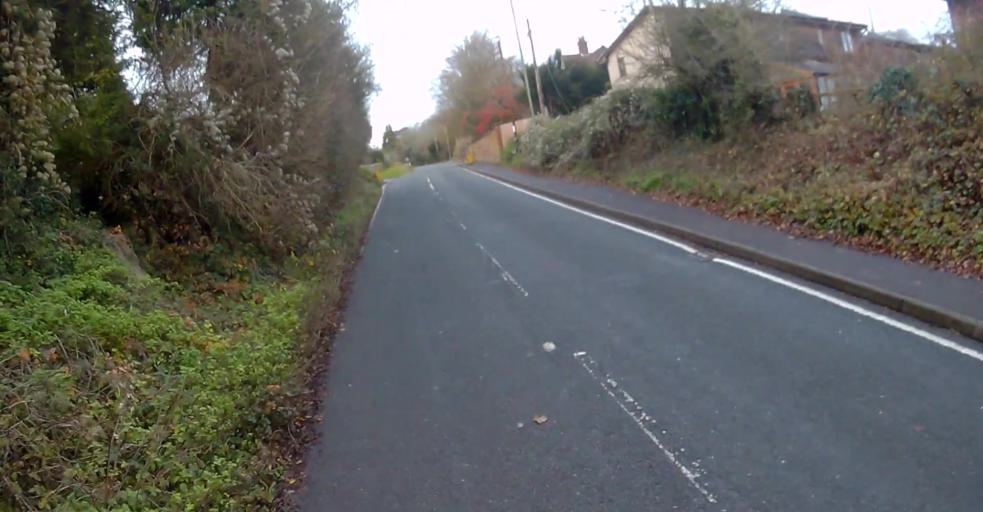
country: GB
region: England
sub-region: Hampshire
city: Overton
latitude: 51.2503
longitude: -1.2639
